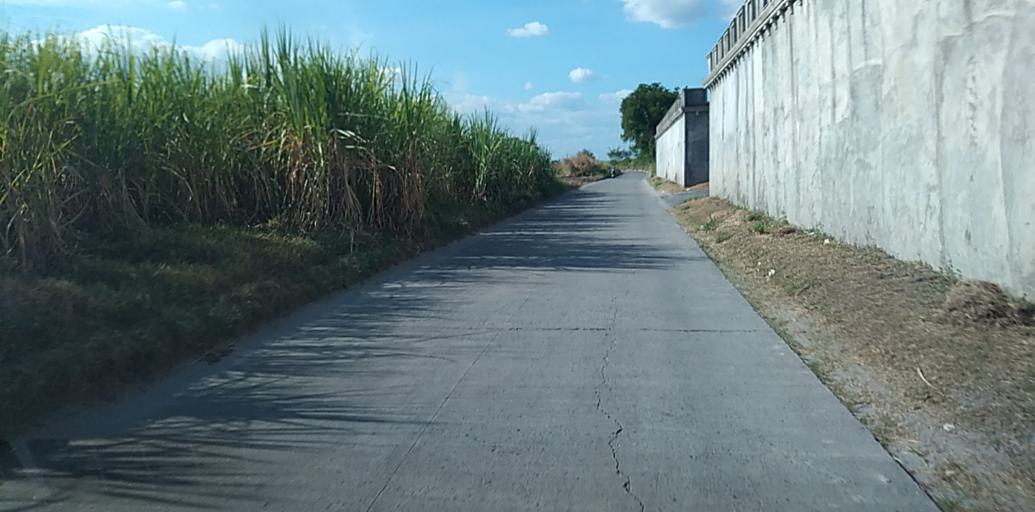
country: PH
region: Central Luzon
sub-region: Province of Pampanga
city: Acli
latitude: 15.1142
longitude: 120.6469
